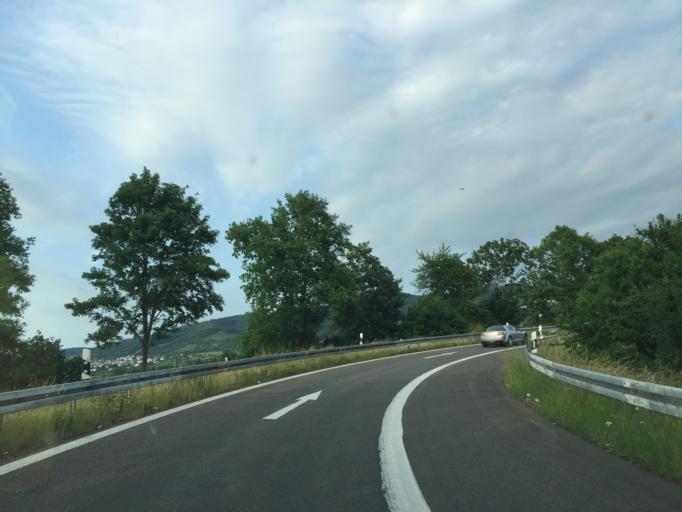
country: DE
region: Baden-Wuerttemberg
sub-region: Karlsruhe Region
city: Schriesheim
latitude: 49.4790
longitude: 8.6408
